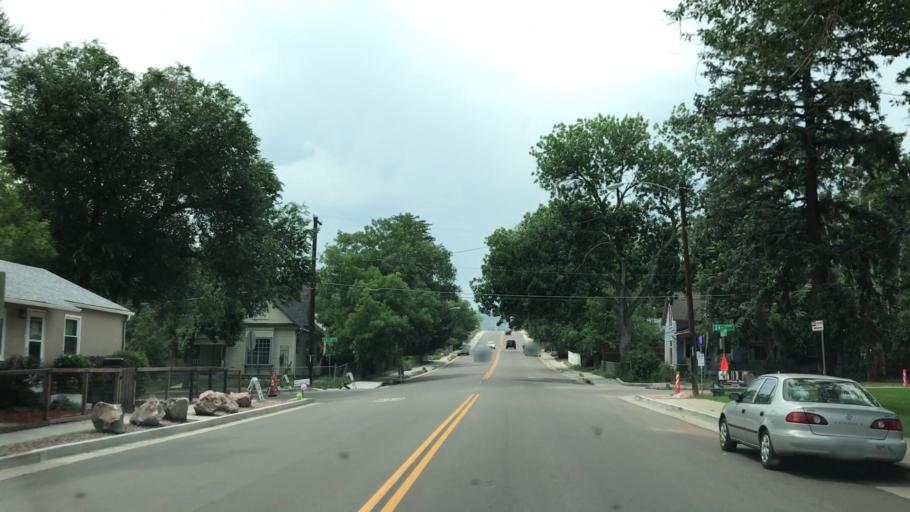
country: US
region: Colorado
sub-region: El Paso County
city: Colorado Springs
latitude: 38.8495
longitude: -104.8574
